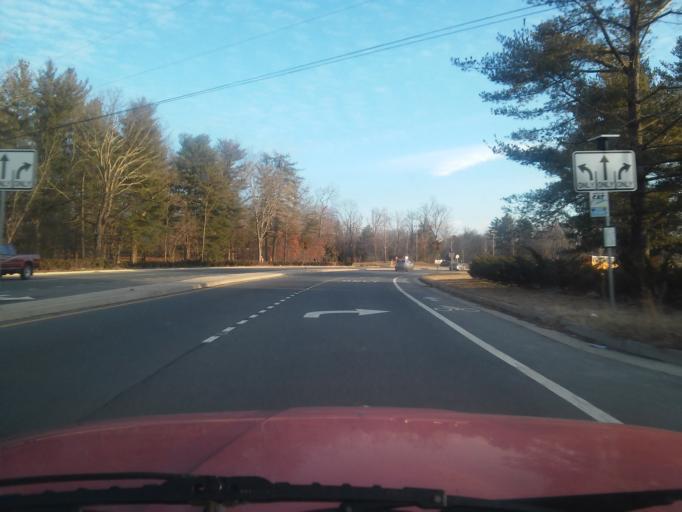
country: US
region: Virginia
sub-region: City of Charlottesville
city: Charlottesville
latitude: 38.0635
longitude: -78.4631
